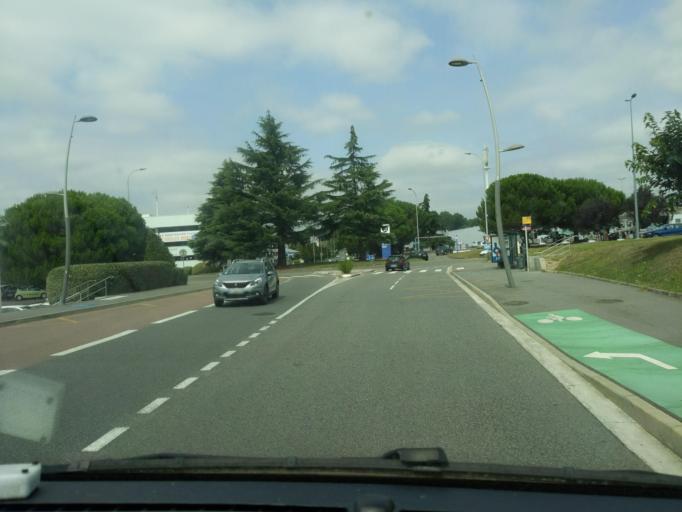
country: FR
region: Midi-Pyrenees
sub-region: Departement de la Haute-Garonne
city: Saint-Orens-de-Gameville
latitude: 43.5647
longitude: 1.5191
